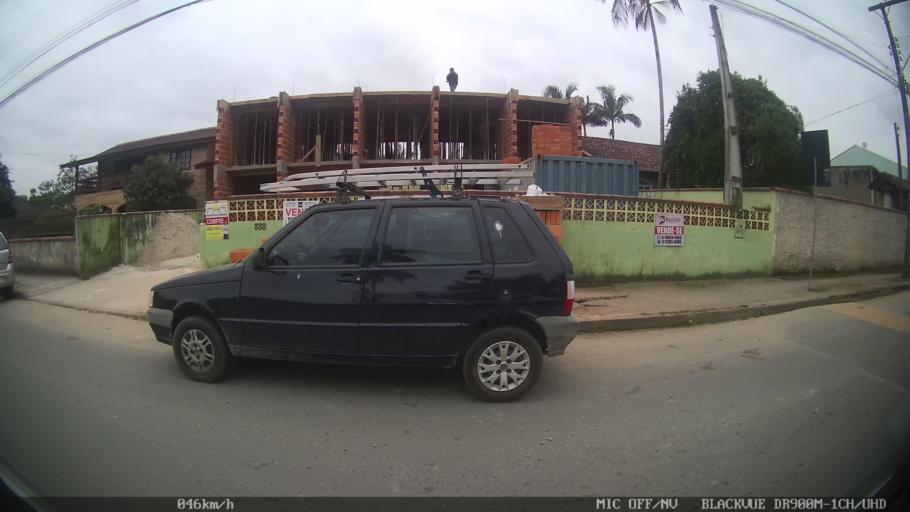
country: BR
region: Santa Catarina
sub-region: Joinville
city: Joinville
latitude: -26.3553
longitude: -48.8279
